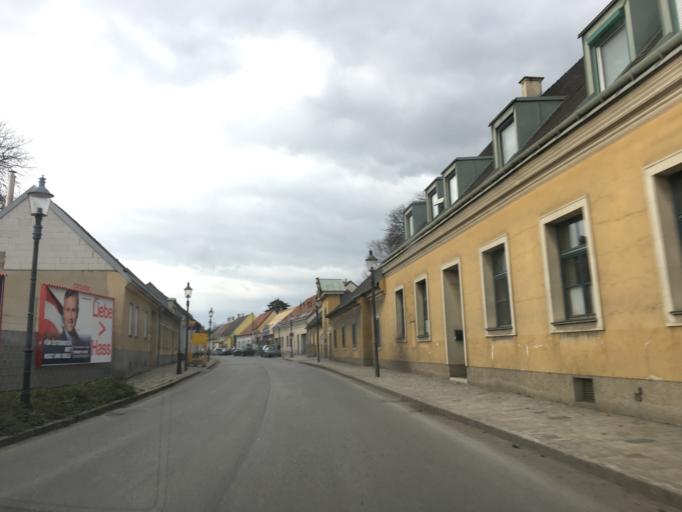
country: AT
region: Lower Austria
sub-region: Politischer Bezirk Wien-Umgebung
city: Gerasdorf bei Wien
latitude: 48.2351
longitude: 16.4658
